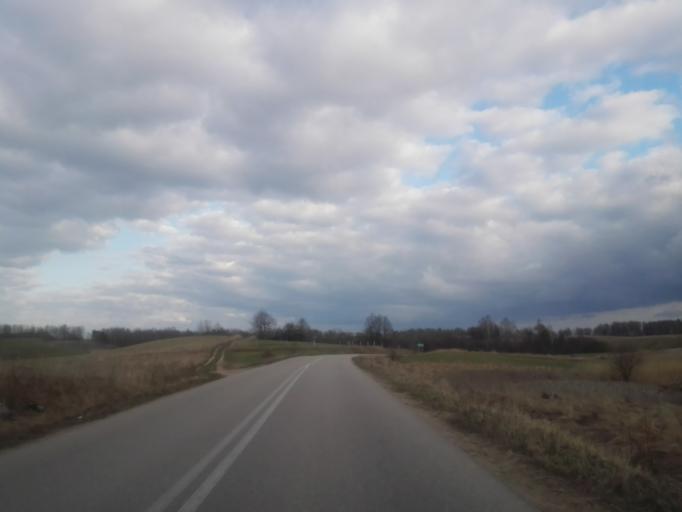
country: PL
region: Podlasie
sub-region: Suwalki
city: Suwalki
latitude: 54.1990
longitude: 22.9942
